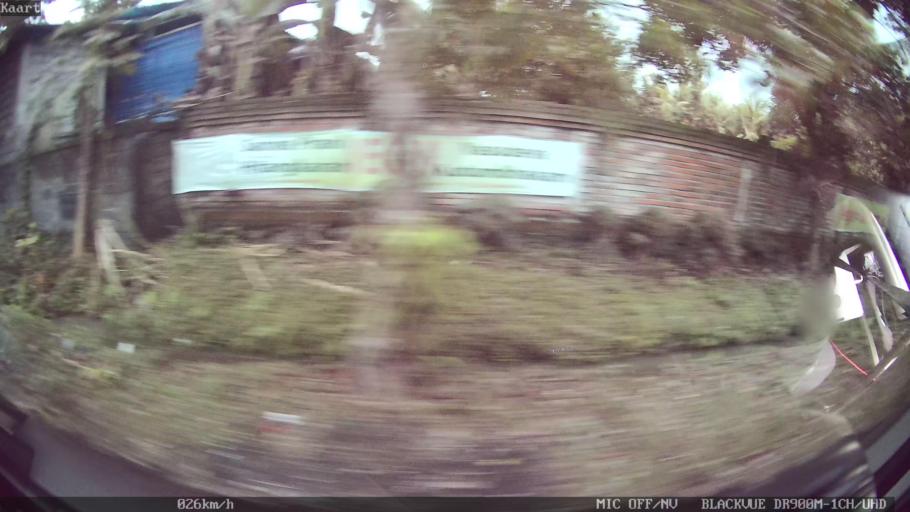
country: ID
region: Bali
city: Banjar Serangan
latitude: -8.5378
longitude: 115.1777
